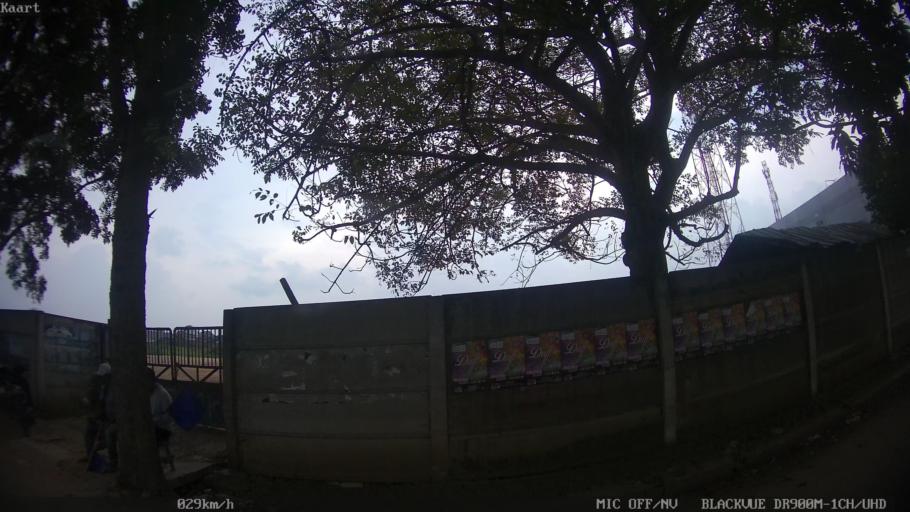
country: ID
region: Lampung
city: Kedaton
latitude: -5.3980
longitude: 105.2813
